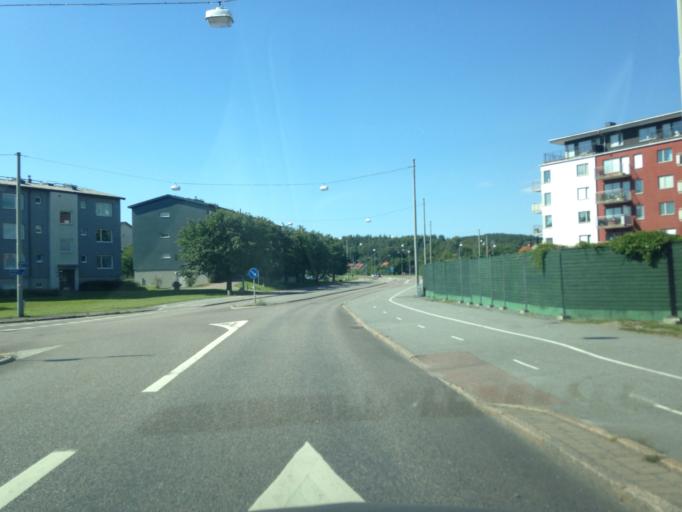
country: SE
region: Vaestra Goetaland
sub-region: Goteborg
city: Majorna
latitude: 57.7169
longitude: 11.9089
